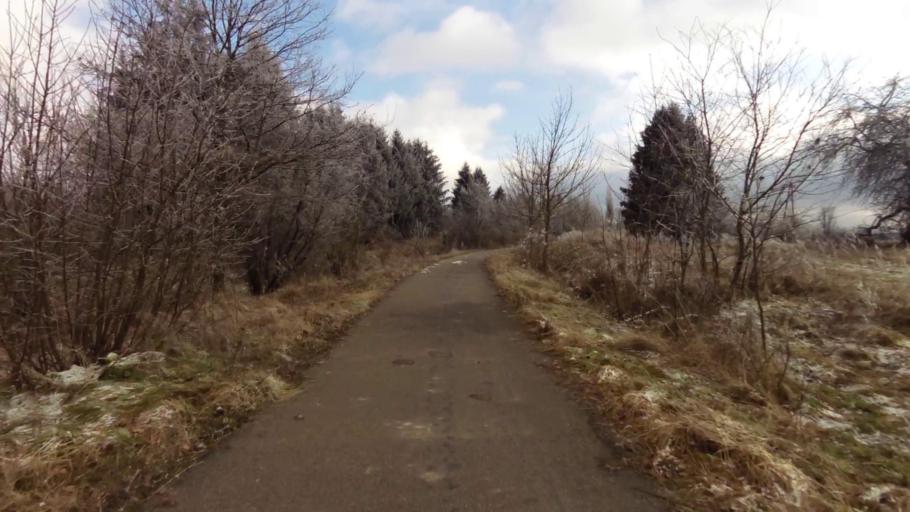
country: PL
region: West Pomeranian Voivodeship
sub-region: Powiat drawski
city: Zlocieniec
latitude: 53.6343
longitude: 16.0542
